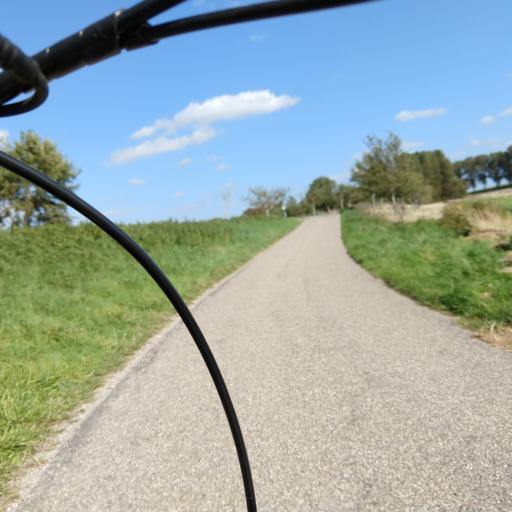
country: NL
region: Zeeland
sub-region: Gemeente Goes
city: Goes
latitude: 51.5574
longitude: 3.8737
